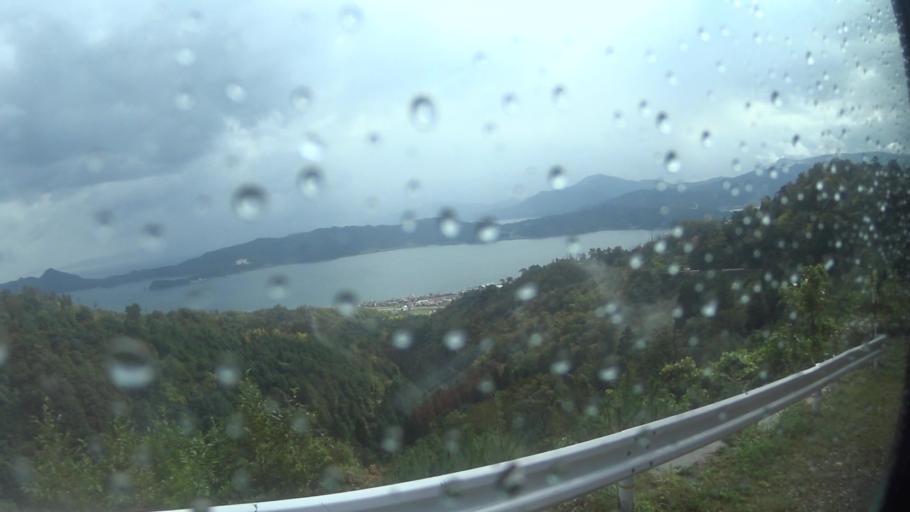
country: JP
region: Kyoto
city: Miyazu
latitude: 35.5907
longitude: 135.1887
